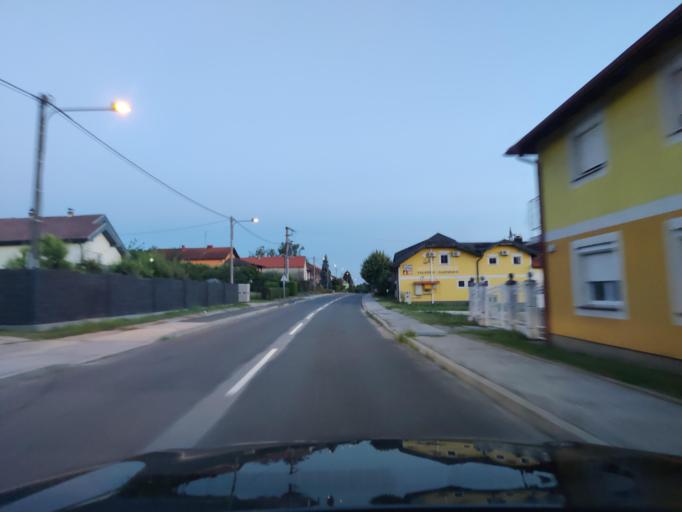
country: SI
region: Lendava-Lendva
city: Lendava
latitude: 46.5815
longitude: 16.4467
